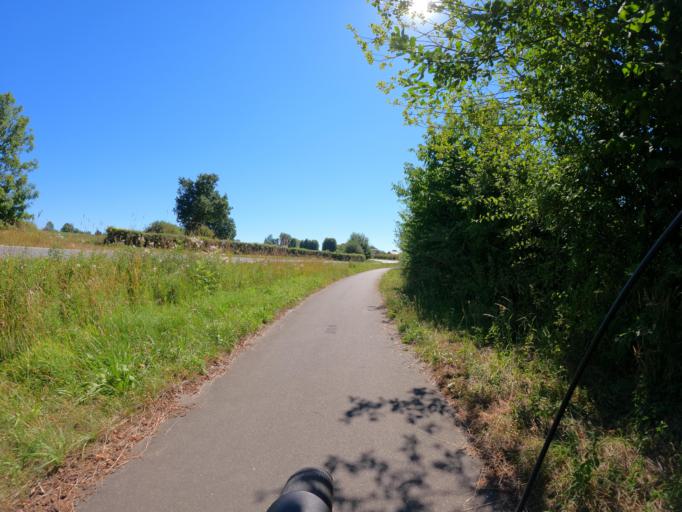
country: DE
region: Schleswig-Holstein
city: Quern
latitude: 54.7856
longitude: 9.7263
